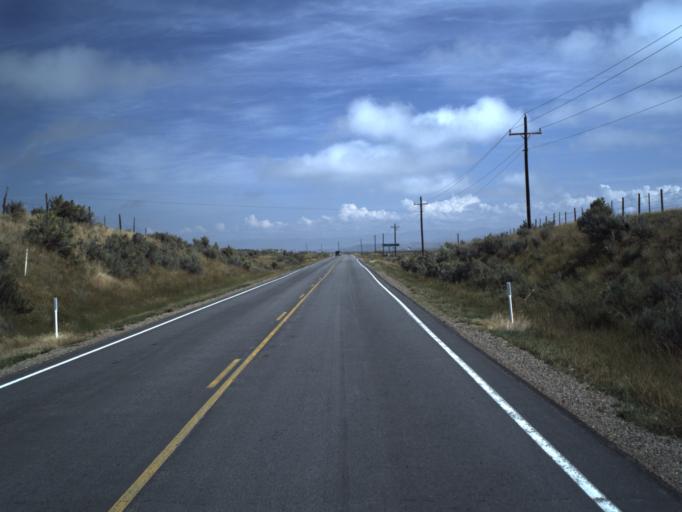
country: US
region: Utah
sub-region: Rich County
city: Randolph
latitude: 41.7611
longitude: -111.1325
